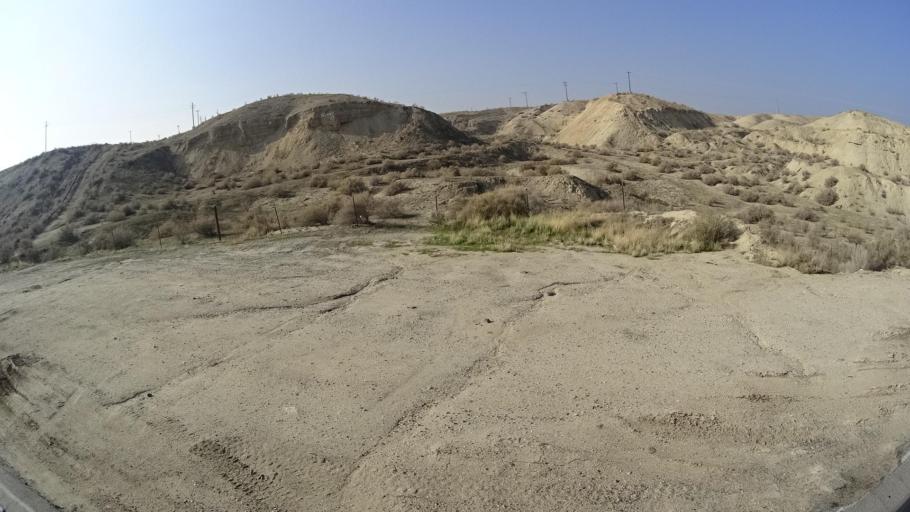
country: US
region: California
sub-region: Kern County
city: Ford City
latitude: 35.2669
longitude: -119.3119
